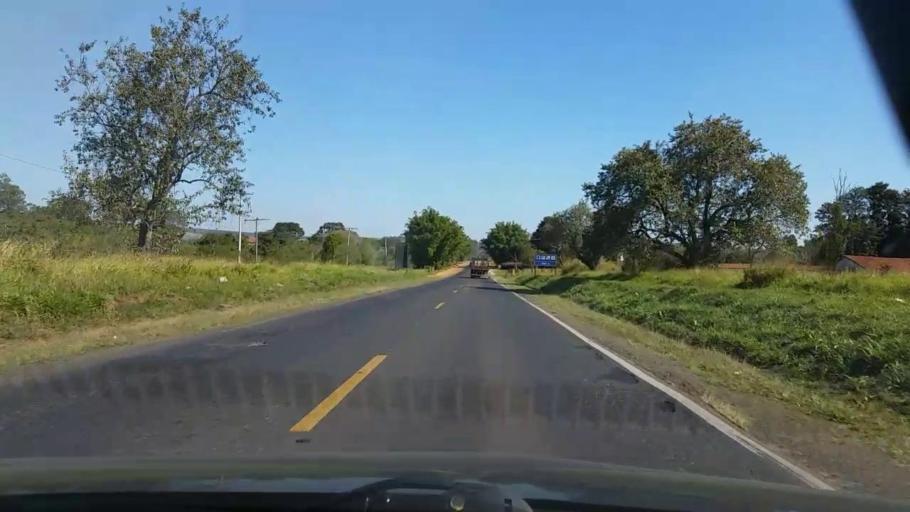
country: BR
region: Sao Paulo
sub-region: Sao Manuel
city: Sao Manuel
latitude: -22.8003
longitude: -48.6646
